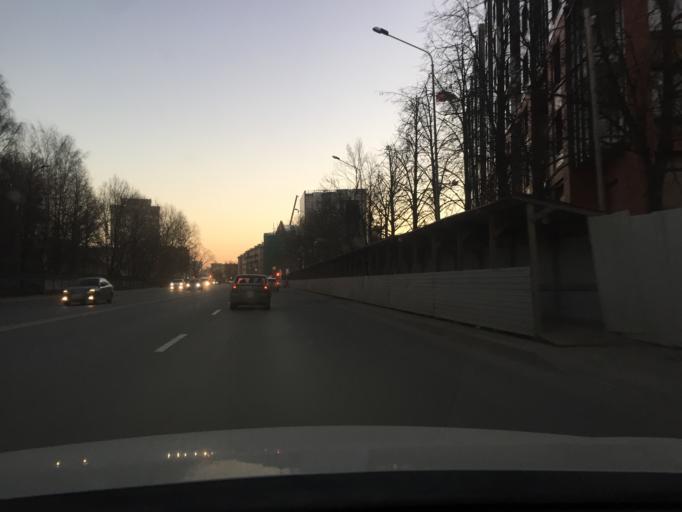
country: RU
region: St.-Petersburg
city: Obukhovo
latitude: 59.8830
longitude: 30.4343
